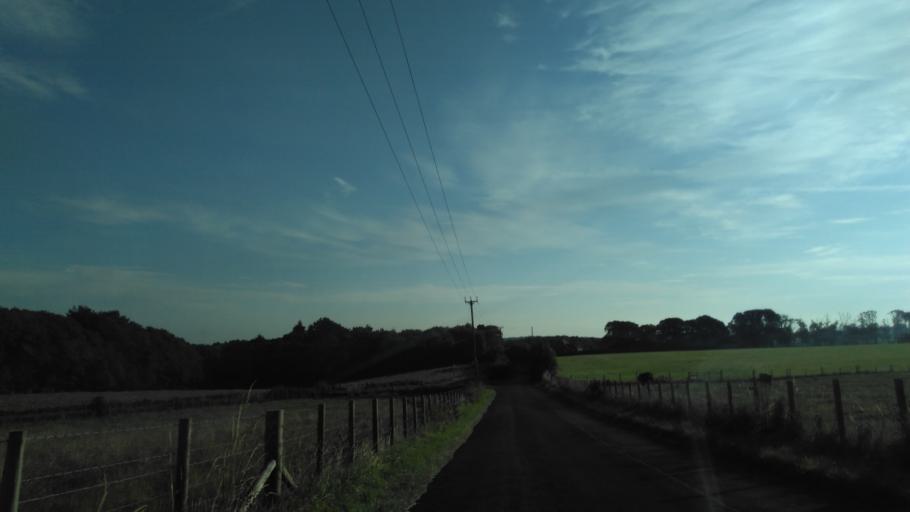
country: GB
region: England
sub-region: Kent
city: Dunkirk
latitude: 51.3019
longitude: 0.9858
